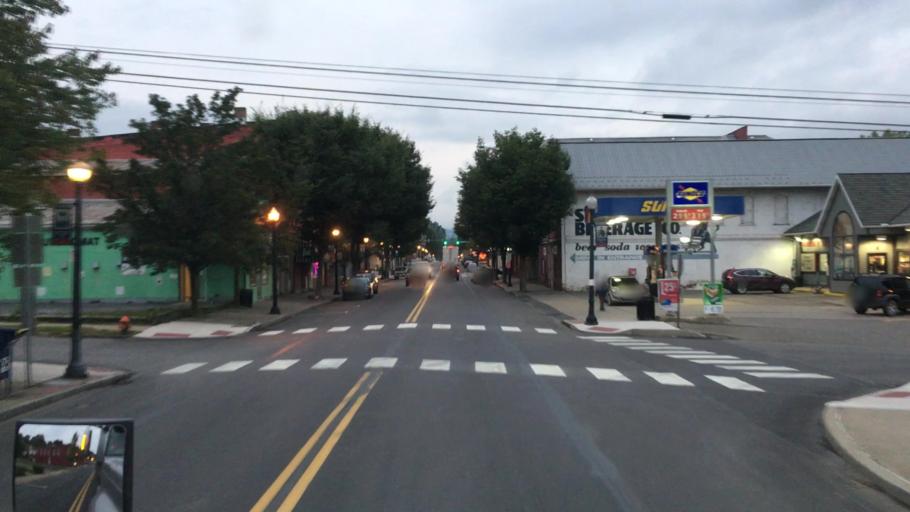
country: US
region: Pennsylvania
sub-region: Bradford County
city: Towanda
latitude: 41.7632
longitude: -76.4431
